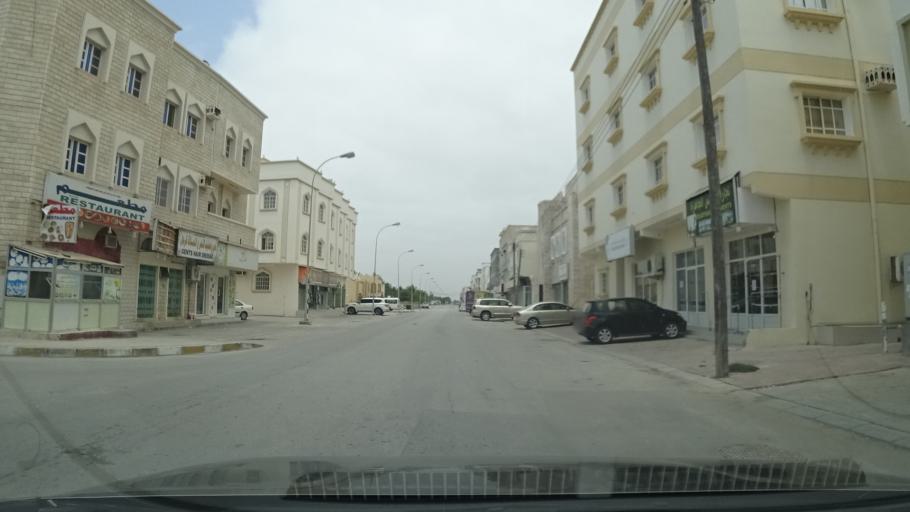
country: OM
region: Zufar
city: Salalah
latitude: 17.0222
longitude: 54.1597
